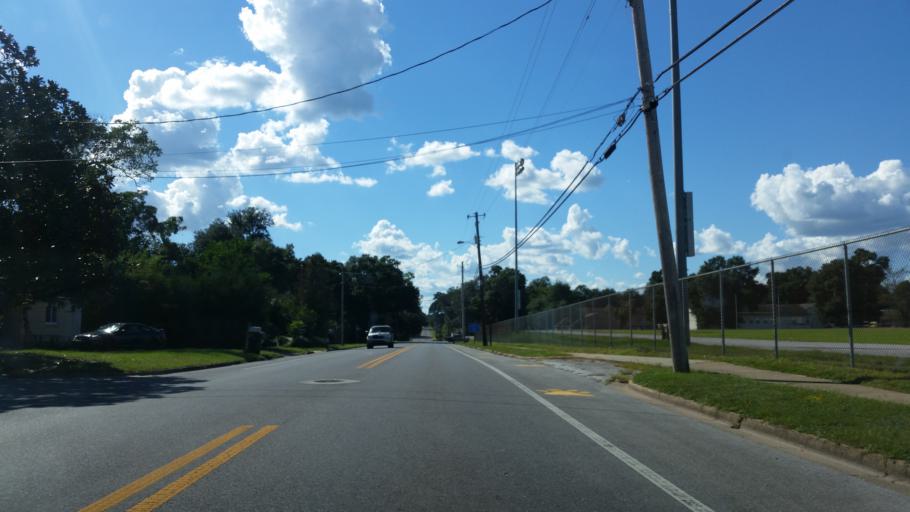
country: US
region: Florida
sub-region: Santa Rosa County
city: Milton
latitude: 30.6309
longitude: -87.0458
